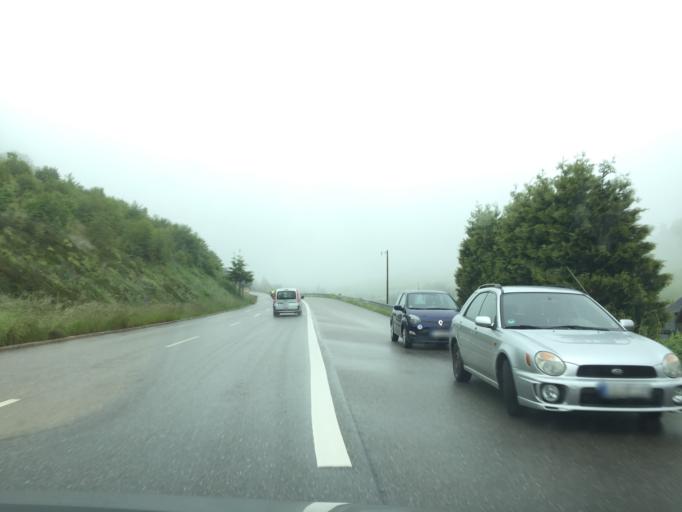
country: DE
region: Baden-Wuerttemberg
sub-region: Freiburg Region
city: Todtnau
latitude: 47.8457
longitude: 7.9377
